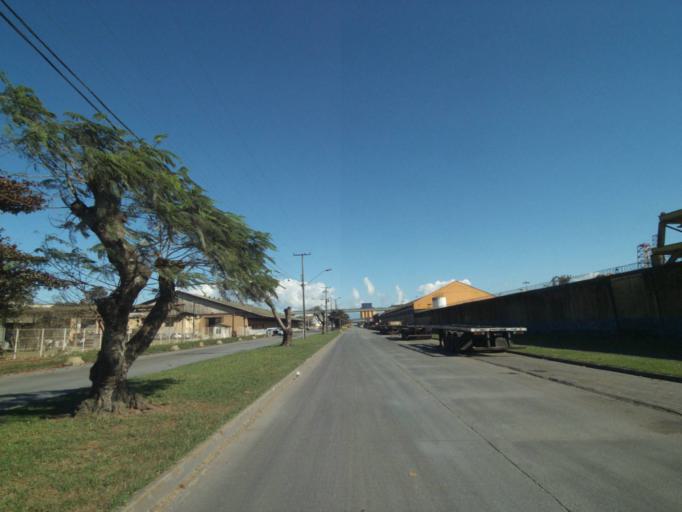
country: BR
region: Parana
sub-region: Paranagua
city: Paranagua
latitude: -25.5039
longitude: -48.5164
